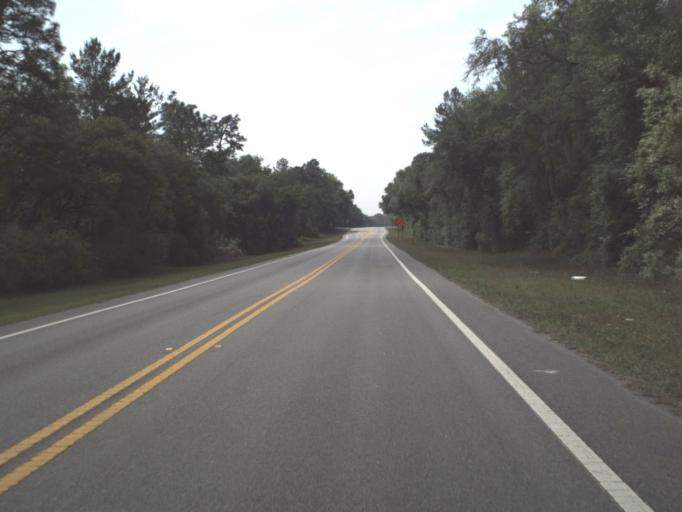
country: US
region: Florida
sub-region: Putnam County
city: Crescent City
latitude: 29.3635
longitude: -81.7355
